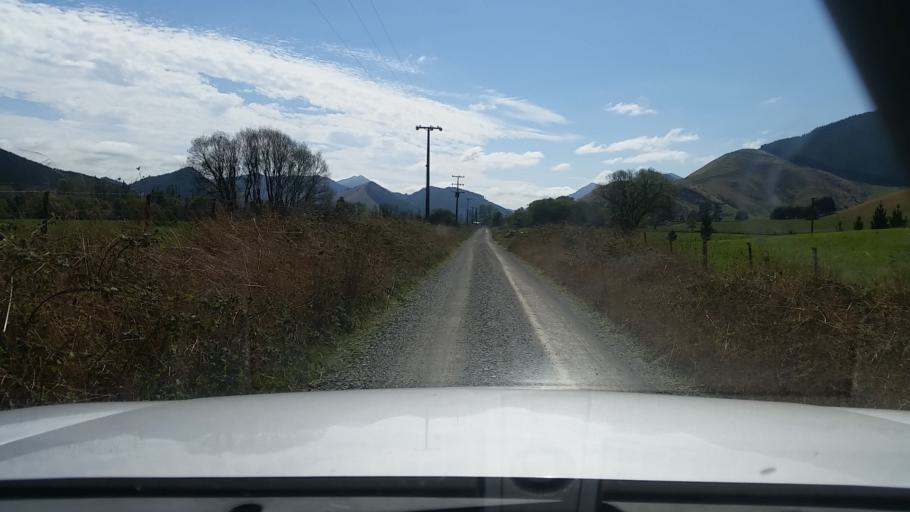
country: NZ
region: Nelson
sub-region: Nelson City
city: Nelson
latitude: -41.2574
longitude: 173.5818
